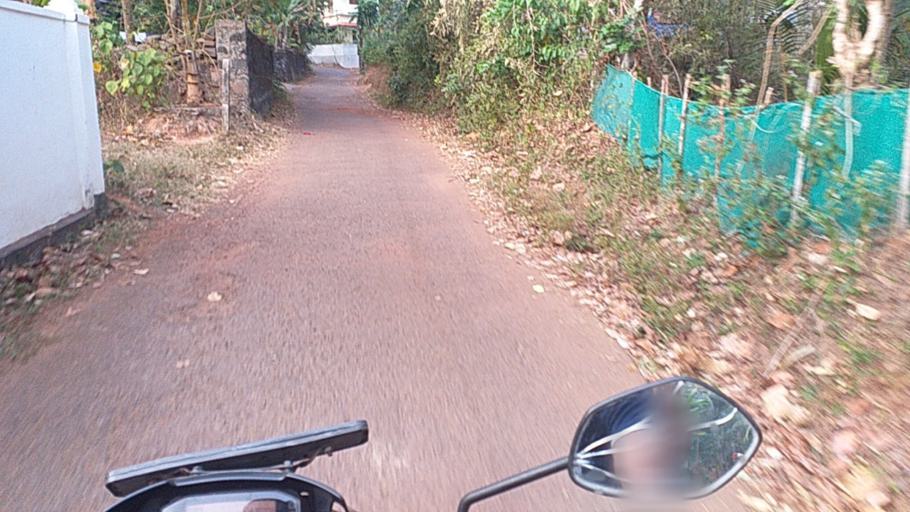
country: IN
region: Kerala
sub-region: Thrissur District
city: Kunnamkulam
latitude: 10.7398
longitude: 76.0411
